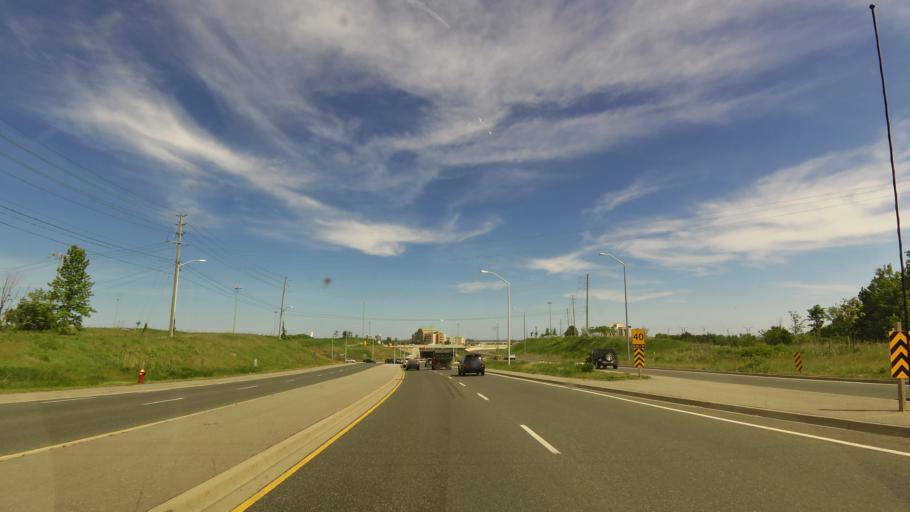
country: CA
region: Ontario
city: Oakville
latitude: 43.4120
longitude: -79.7434
